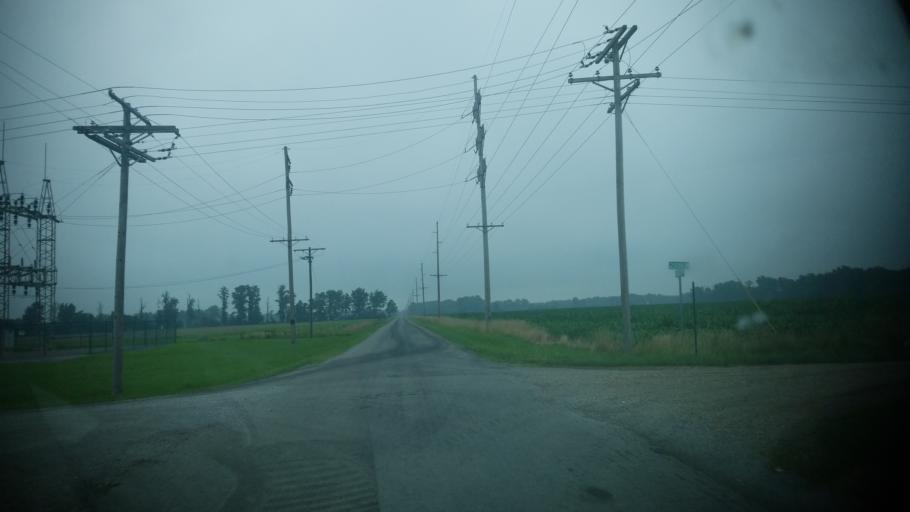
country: US
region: Illinois
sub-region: Clay County
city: Flora
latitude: 38.5444
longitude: -88.4020
